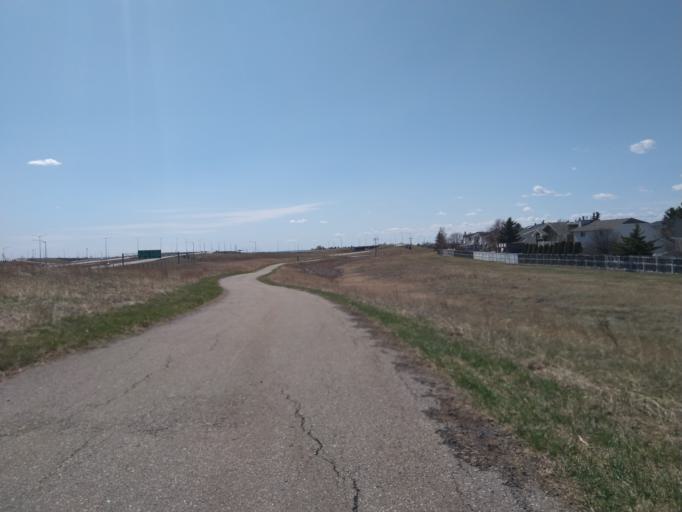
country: CA
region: Alberta
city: Chestermere
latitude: 51.0738
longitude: -113.9223
